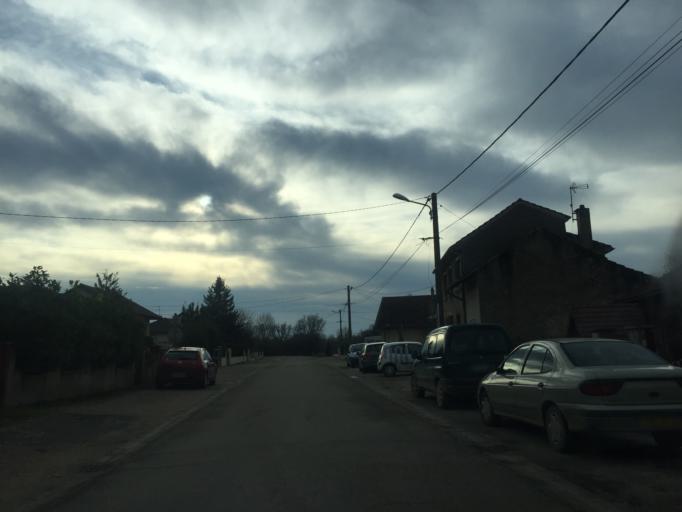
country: FR
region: Franche-Comte
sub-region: Departement du Jura
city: Tavaux
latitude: 47.0156
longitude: 5.4208
